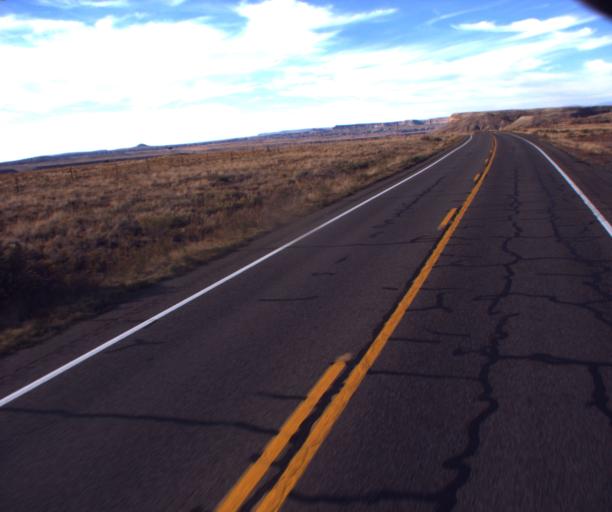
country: US
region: New Mexico
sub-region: San Juan County
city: Shiprock
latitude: 36.9103
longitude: -109.0726
